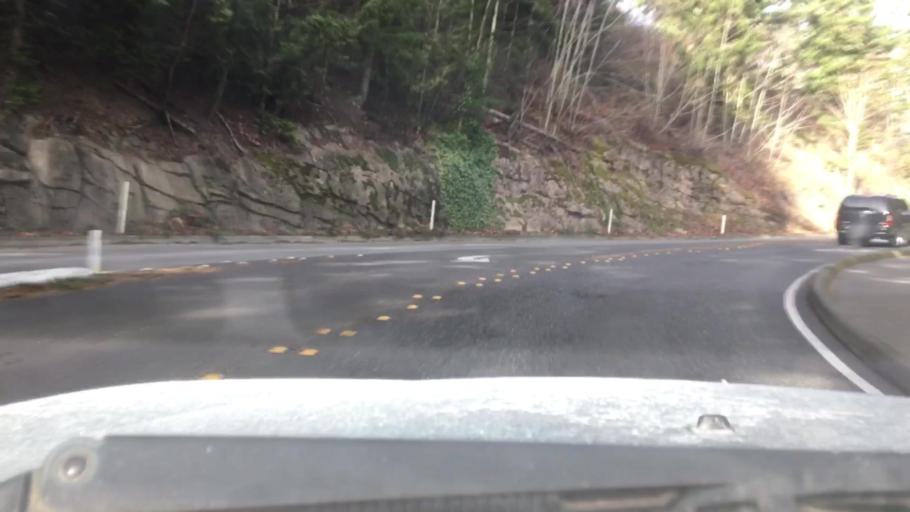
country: US
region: Washington
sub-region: Whatcom County
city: Bellingham
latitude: 48.7314
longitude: -122.4908
